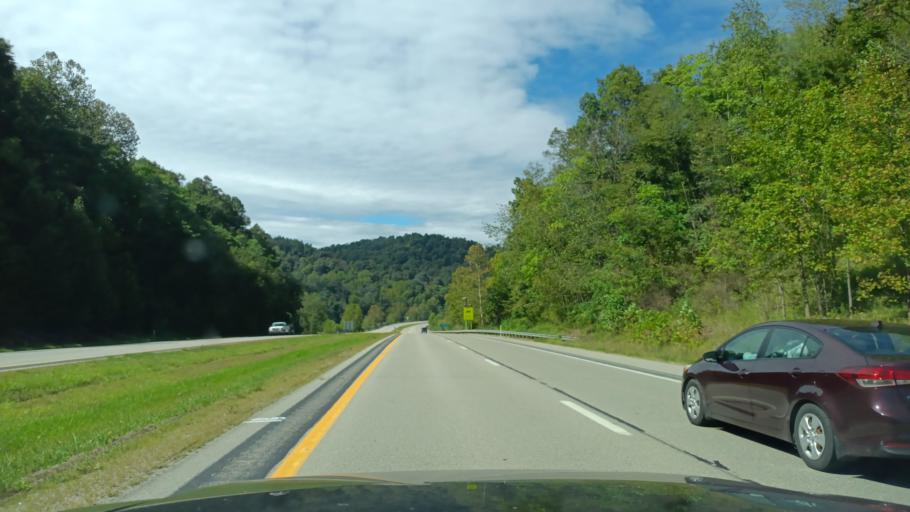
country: US
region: West Virginia
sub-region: Doddridge County
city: West Union
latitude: 39.2881
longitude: -80.7370
